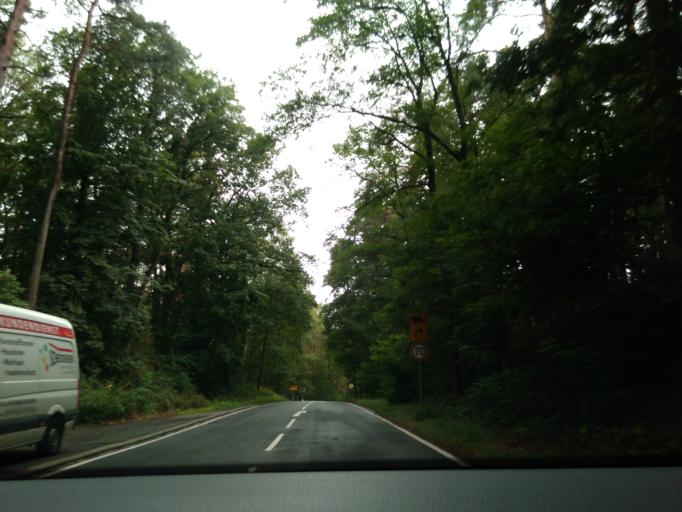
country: DE
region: Bavaria
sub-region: Regierungsbezirk Mittelfranken
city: Cadolzburg
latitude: 49.4566
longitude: 10.8756
